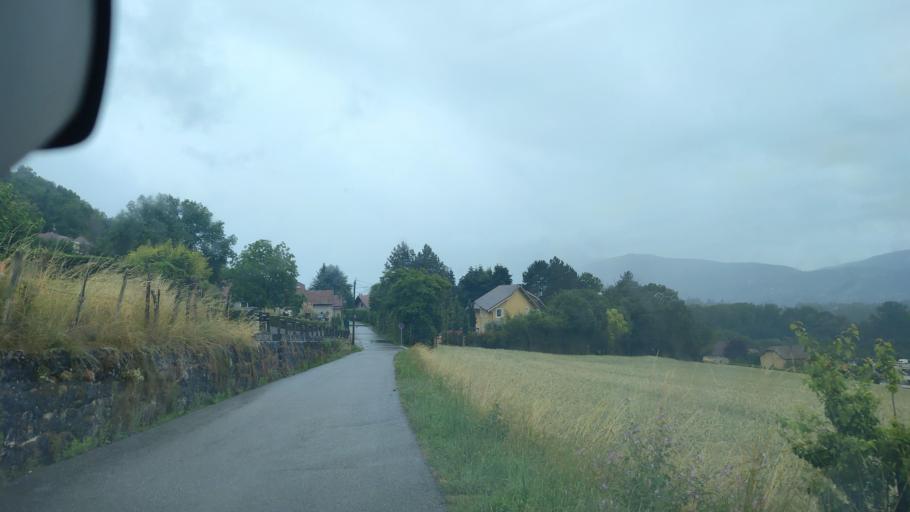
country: FR
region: Rhone-Alpes
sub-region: Departement de la Savoie
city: Chindrieux
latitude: 45.8152
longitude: 5.8526
